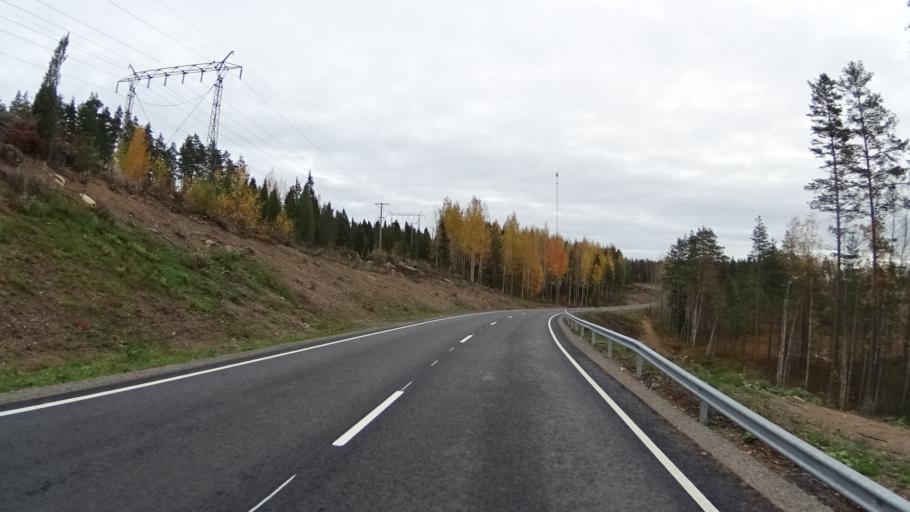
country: FI
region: South Karelia
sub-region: Lappeenranta
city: Luumaeki
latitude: 60.9371
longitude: 27.6670
